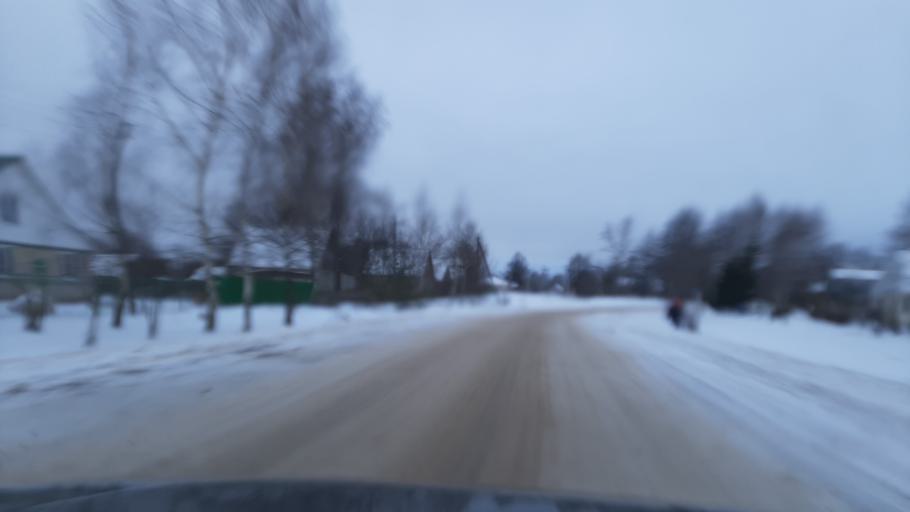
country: RU
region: Kostroma
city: Volgorechensk
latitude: 57.4346
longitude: 41.0709
